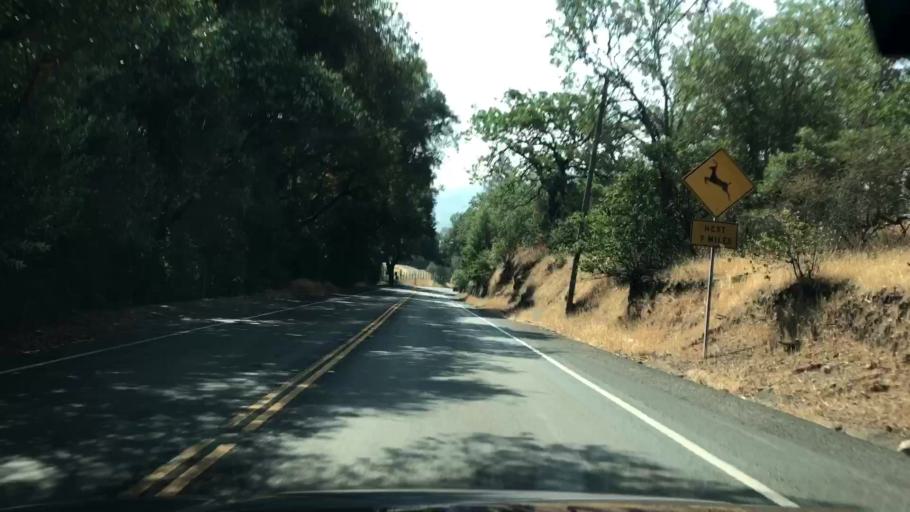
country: US
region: California
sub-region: Napa County
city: Calistoga
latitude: 38.5651
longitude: -122.6256
